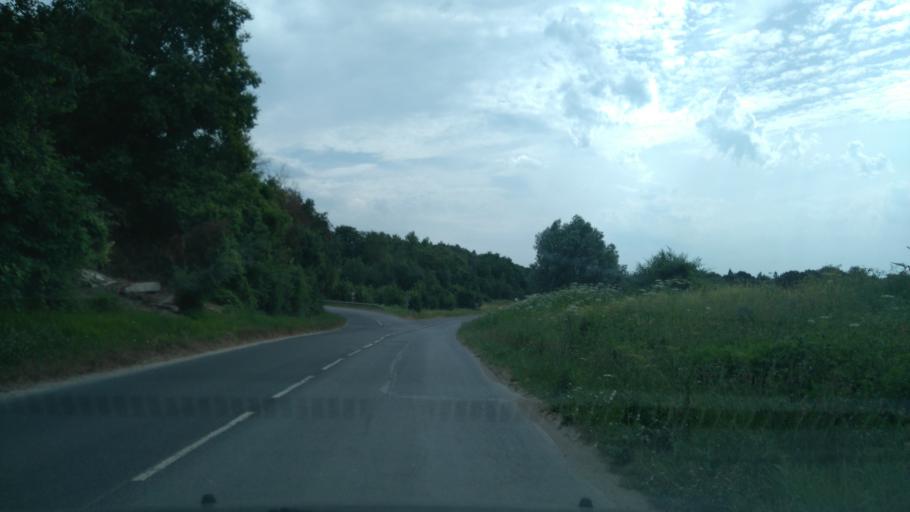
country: FR
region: Picardie
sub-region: Departement de l'Oise
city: Saint-Maximin
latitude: 49.2139
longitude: 2.4319
